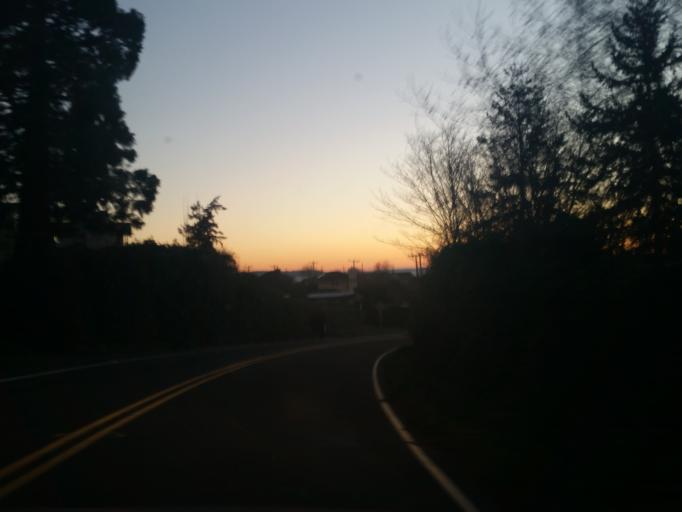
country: US
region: Washington
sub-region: Snohomish County
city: Woodway
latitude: 47.7746
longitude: -122.3916
